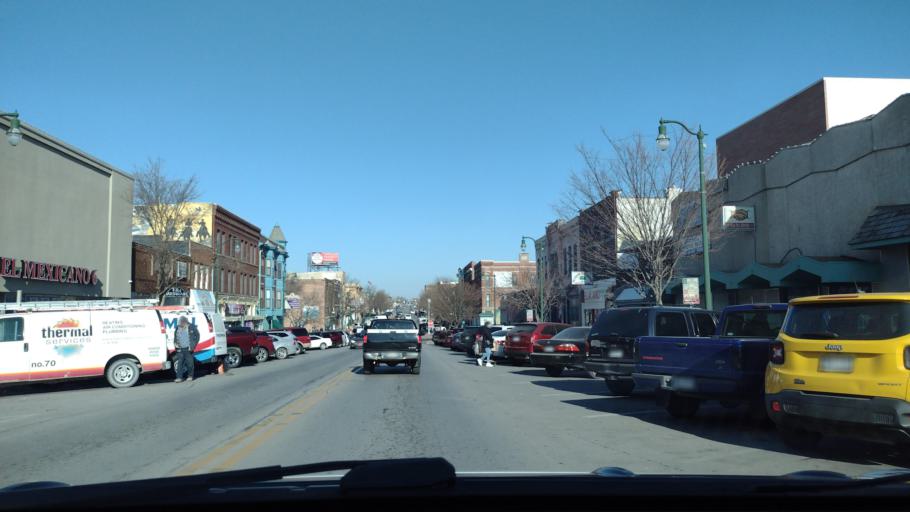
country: US
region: Nebraska
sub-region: Douglas County
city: Omaha
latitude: 41.2087
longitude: -95.9471
